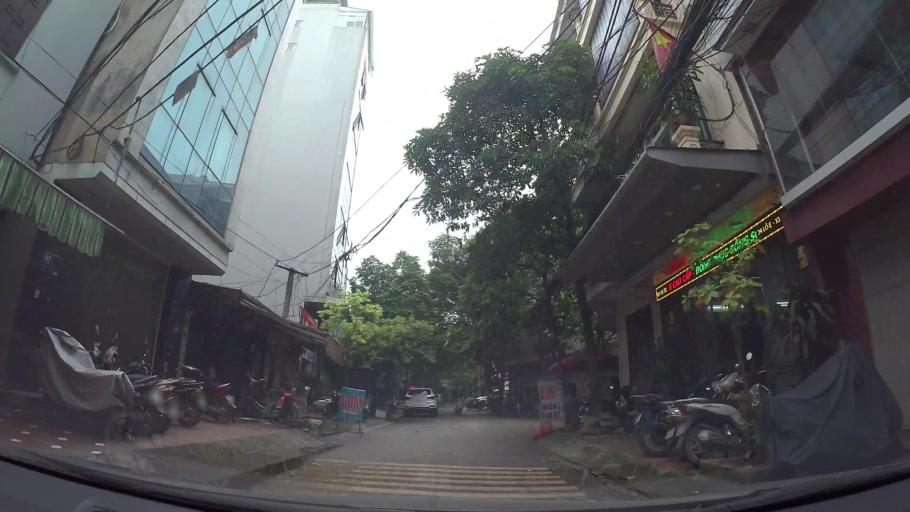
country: VN
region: Ha Noi
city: Van Dien
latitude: 20.9675
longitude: 105.8444
